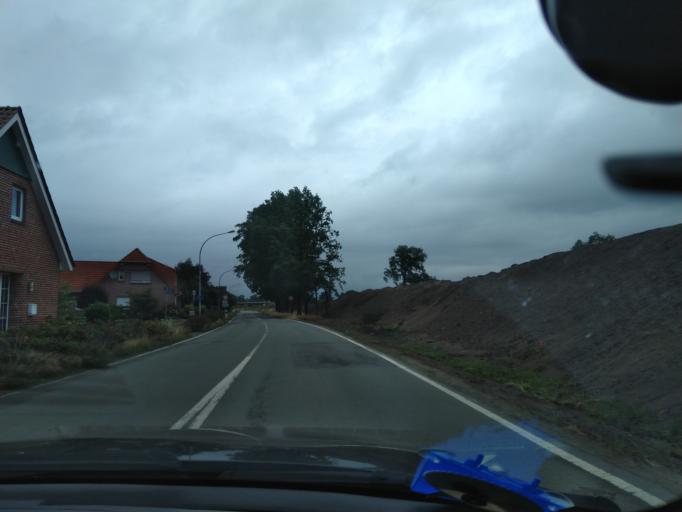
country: DE
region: Lower Saxony
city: Nordhorn
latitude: 52.4449
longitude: 7.0858
